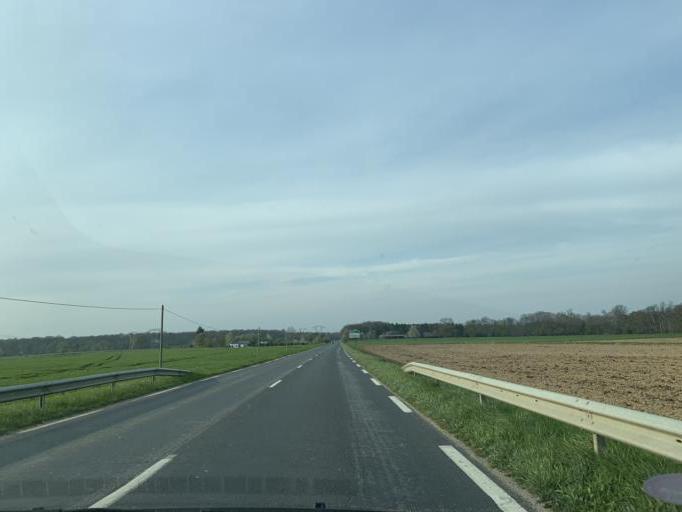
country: FR
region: Haute-Normandie
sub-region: Departement de l'Eure
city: Hauville
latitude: 49.4056
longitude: 0.7971
